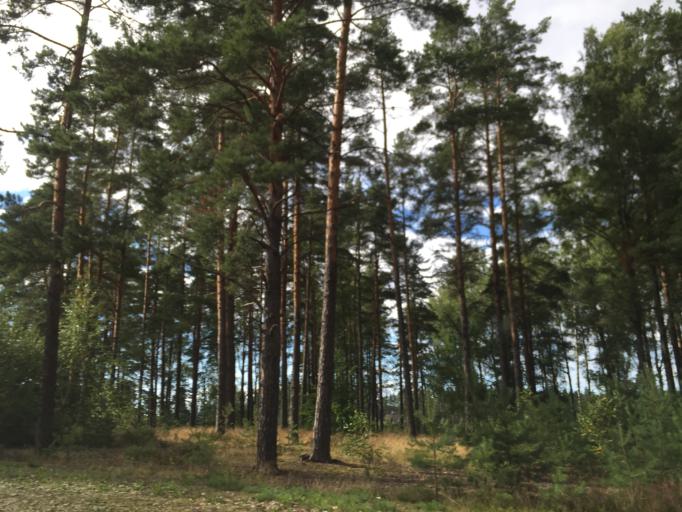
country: LV
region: Saulkrastu
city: Saulkrasti
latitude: 57.1767
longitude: 24.3729
